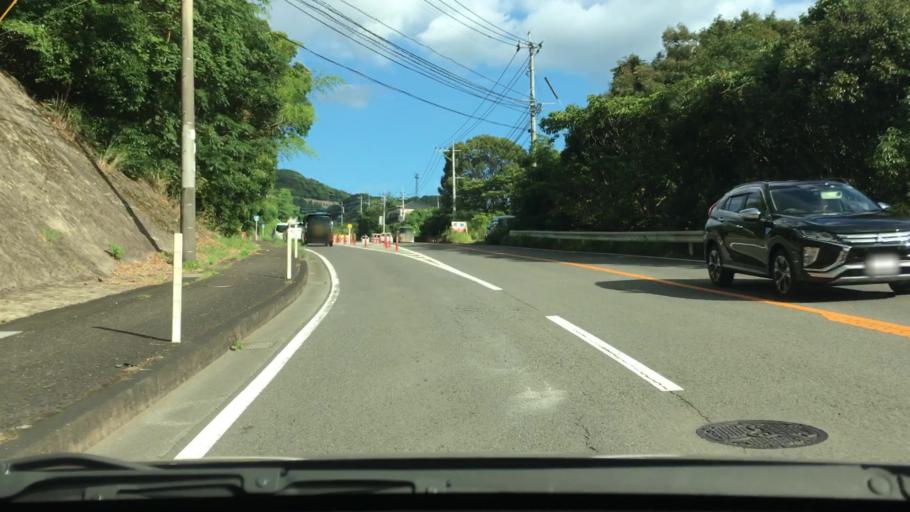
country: JP
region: Nagasaki
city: Togitsu
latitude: 32.8196
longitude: 129.8010
